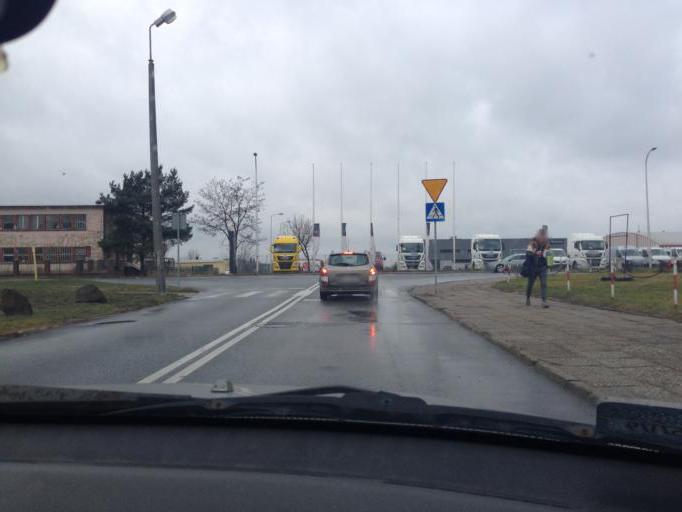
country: PL
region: Opole Voivodeship
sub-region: Powiat opolski
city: Opole
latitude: 50.6834
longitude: 17.9430
